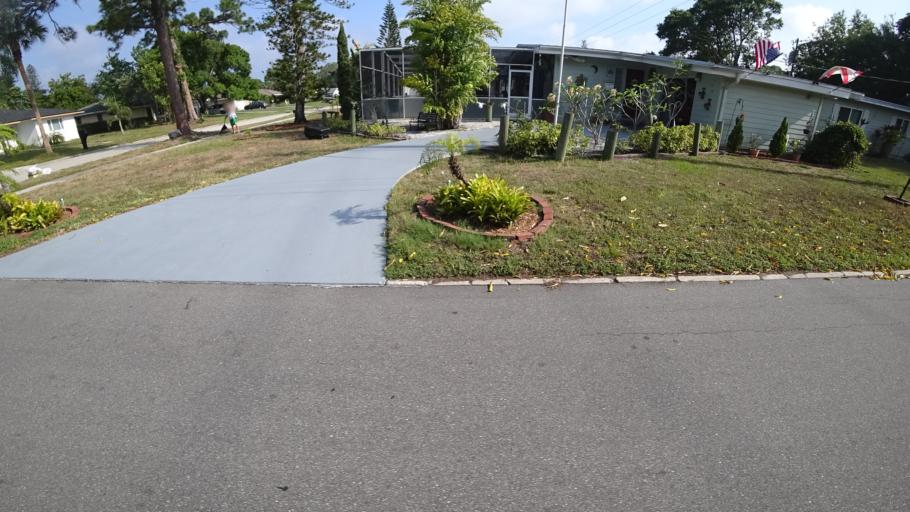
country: US
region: Florida
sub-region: Manatee County
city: West Bradenton
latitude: 27.4976
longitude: -82.6068
